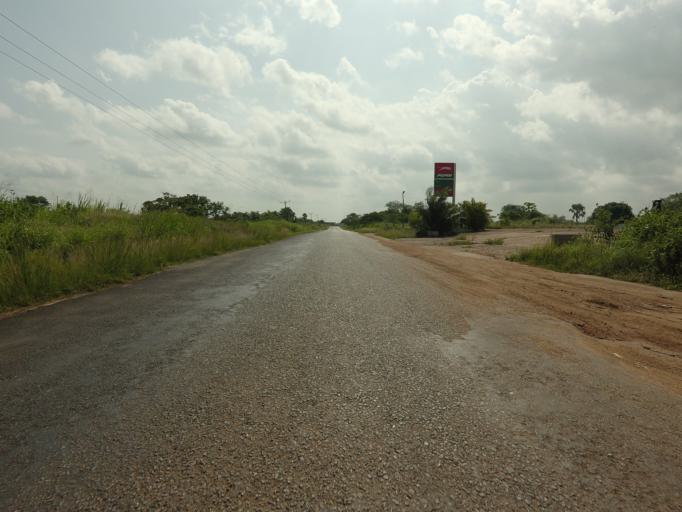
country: GH
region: Volta
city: Ho
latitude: 6.4078
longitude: 0.7704
